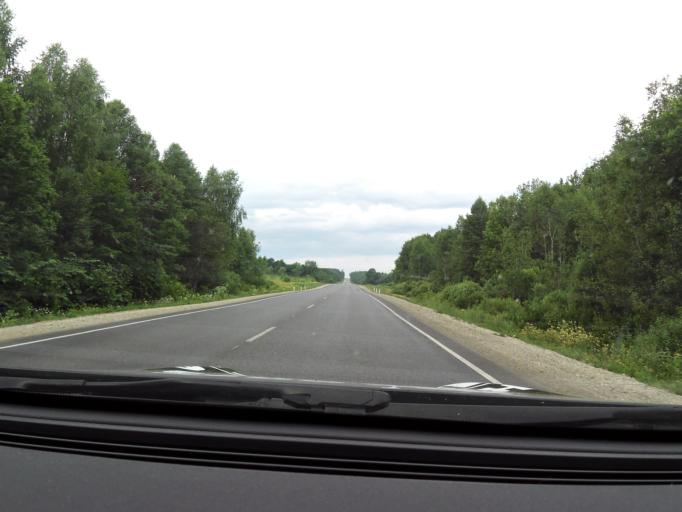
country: RU
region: Bashkortostan
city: Ulu-Telyak
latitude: 54.8462
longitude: 57.0949
